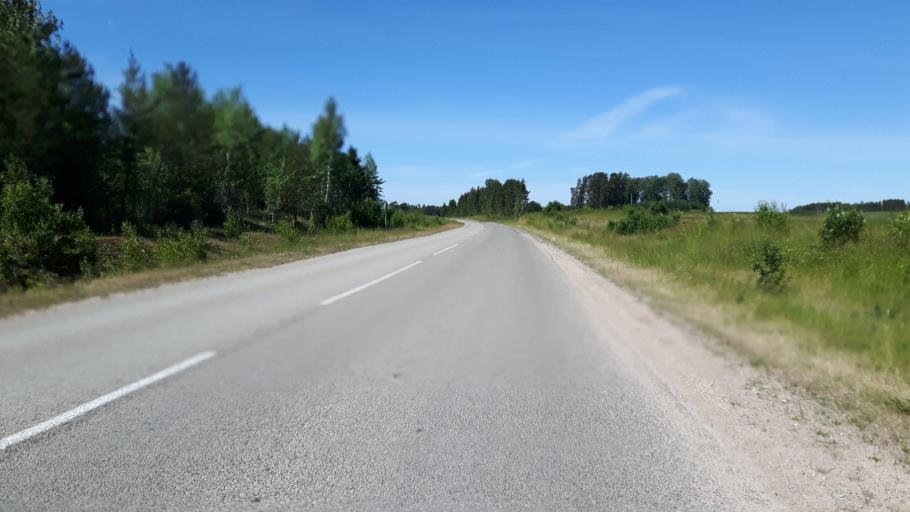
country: LV
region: Tukuma Rajons
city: Tukums
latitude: 57.0166
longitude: 23.0321
